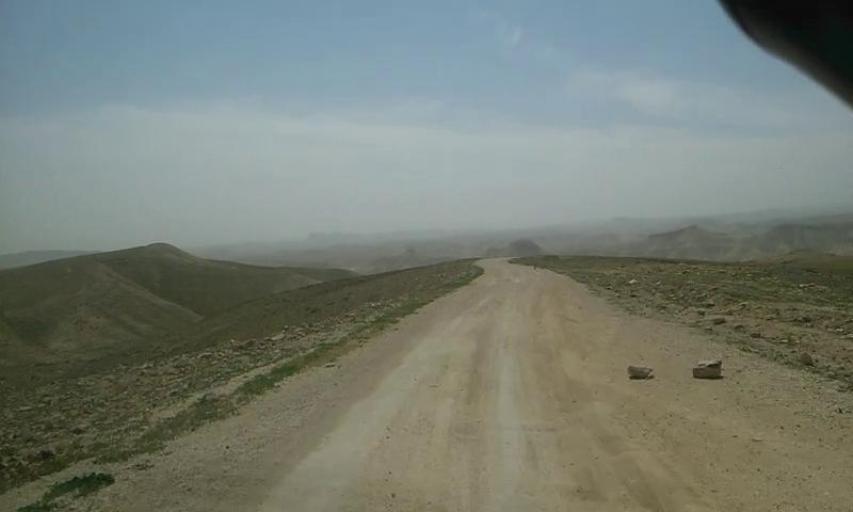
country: PS
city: `Arab ar Rashaydah
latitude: 31.5190
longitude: 35.2964
